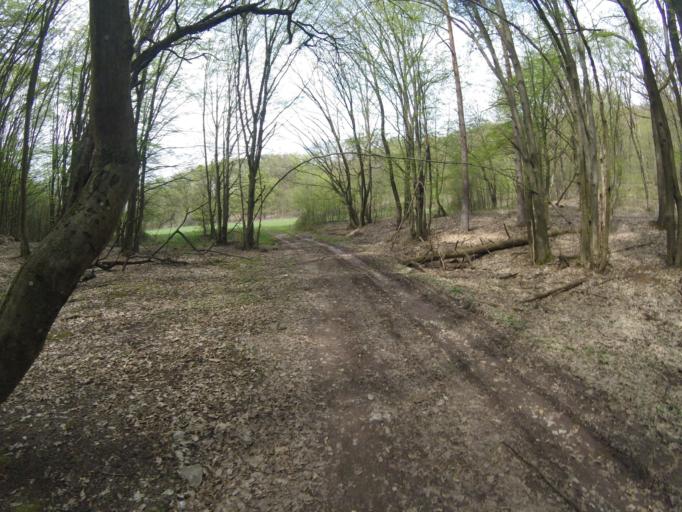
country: SK
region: Kosicky
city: Roznava
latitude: 48.5486
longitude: 20.6582
